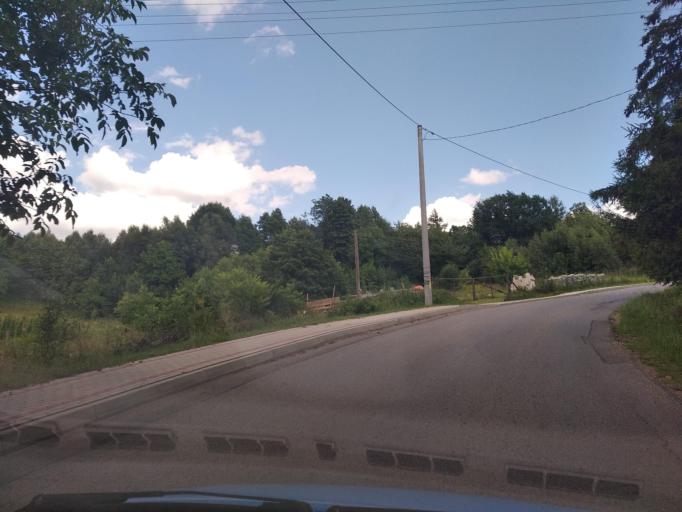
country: PL
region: Subcarpathian Voivodeship
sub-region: Powiat strzyzowski
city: Polomia
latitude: 49.9237
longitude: 21.9042
